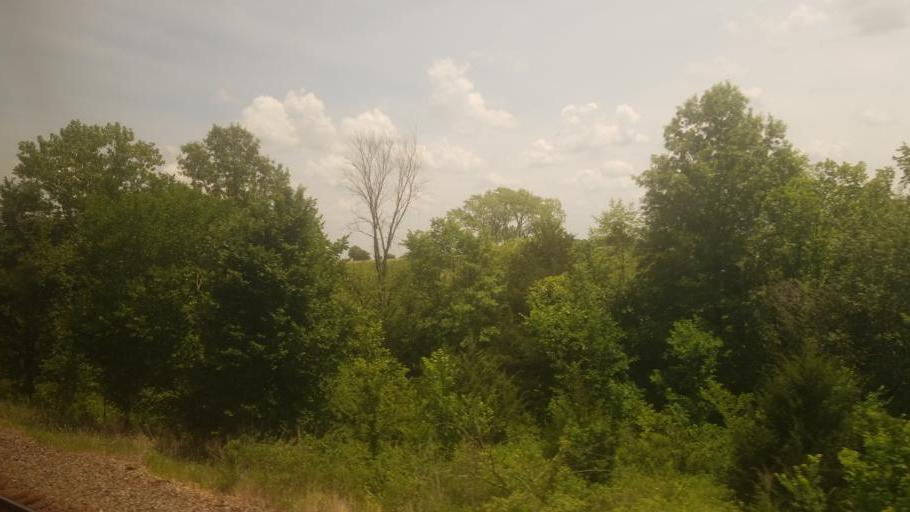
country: US
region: Missouri
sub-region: Macon County
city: La Plata
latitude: 40.0927
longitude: -92.4187
